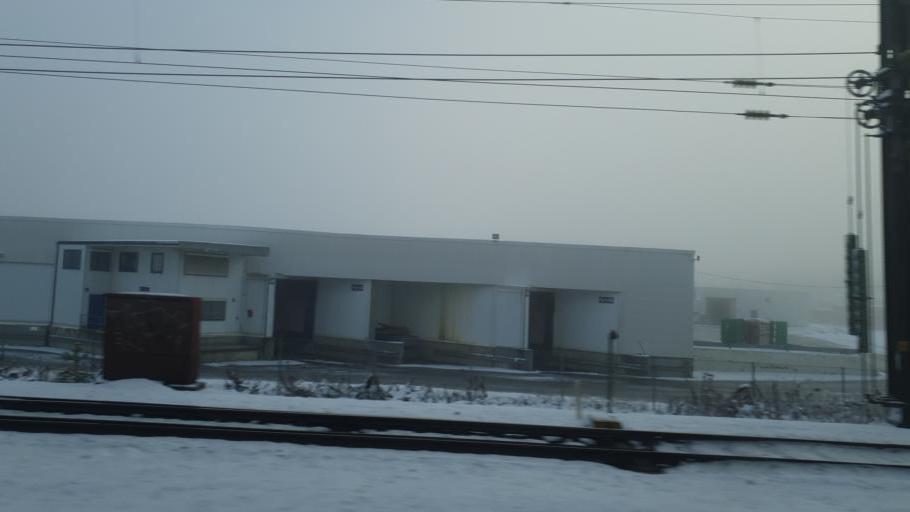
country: NO
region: Akershus
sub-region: Skedsmo
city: Lillestrom
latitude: 59.9661
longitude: 11.0665
